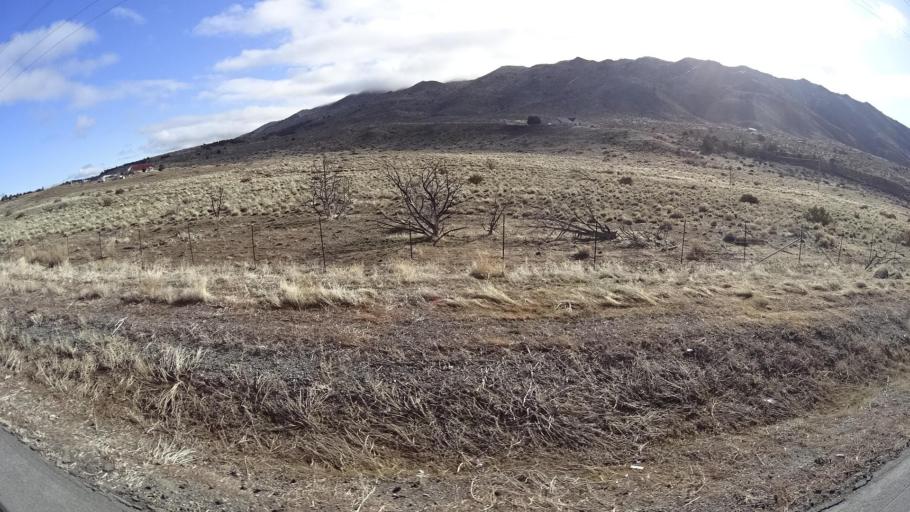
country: US
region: Nevada
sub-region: Washoe County
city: Cold Springs
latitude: 39.7687
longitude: -119.8869
